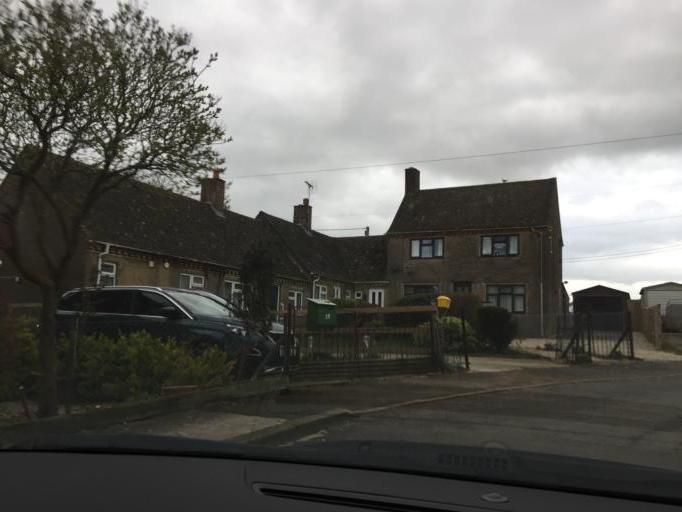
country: GB
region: England
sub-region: Oxfordshire
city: Chipping Norton
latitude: 51.9534
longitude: -1.5449
